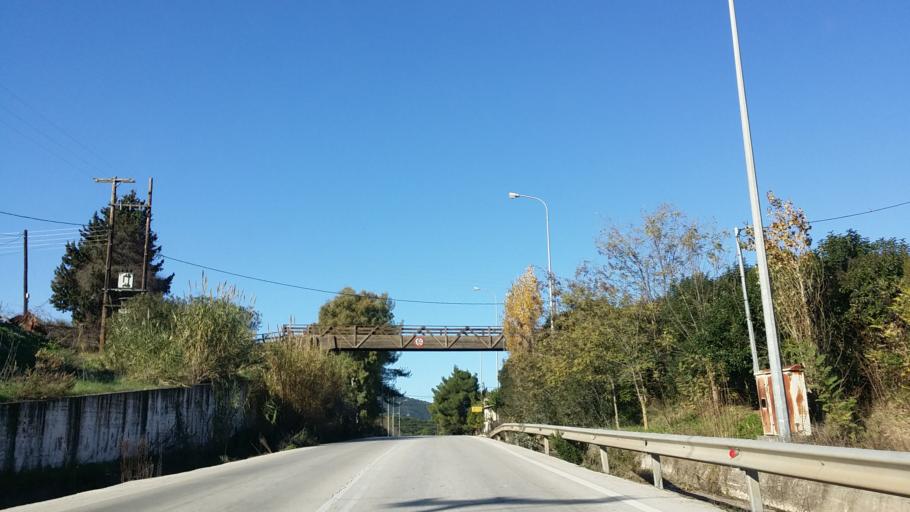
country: GR
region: West Greece
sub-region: Nomos Aitolias kai Akarnanias
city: Monastirakion
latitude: 38.9090
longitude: 20.9524
